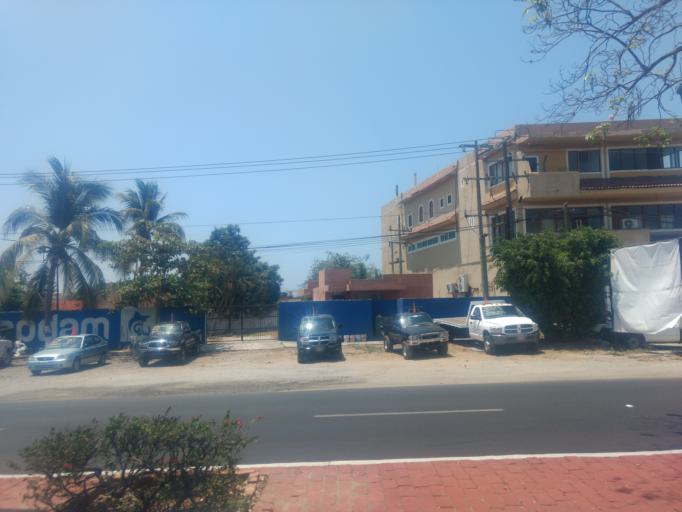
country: MX
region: Colima
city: Tapeixtles
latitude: 19.0855
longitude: -104.3065
